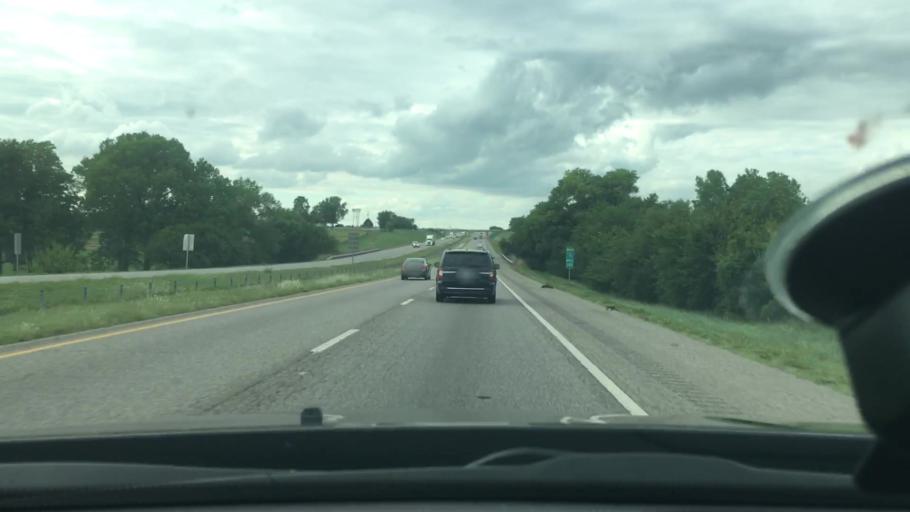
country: US
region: Oklahoma
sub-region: McClain County
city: Goldsby
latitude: 35.1115
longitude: -97.4381
